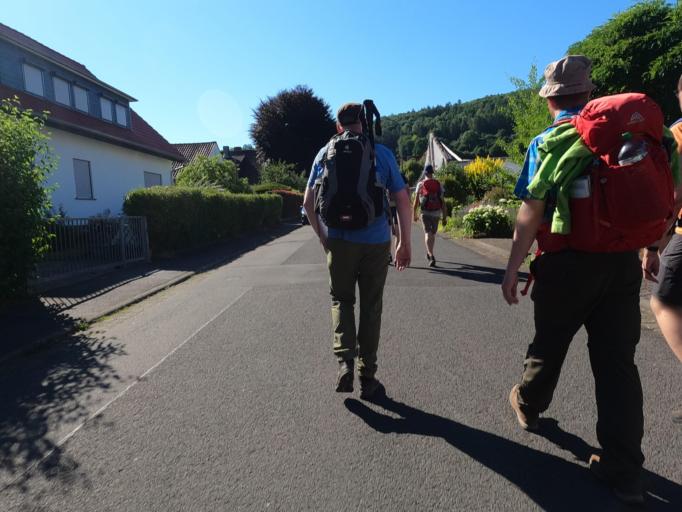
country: DE
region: Hesse
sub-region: Regierungsbezirk Darmstadt
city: Schluchtern
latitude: 50.3446
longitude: 9.5309
